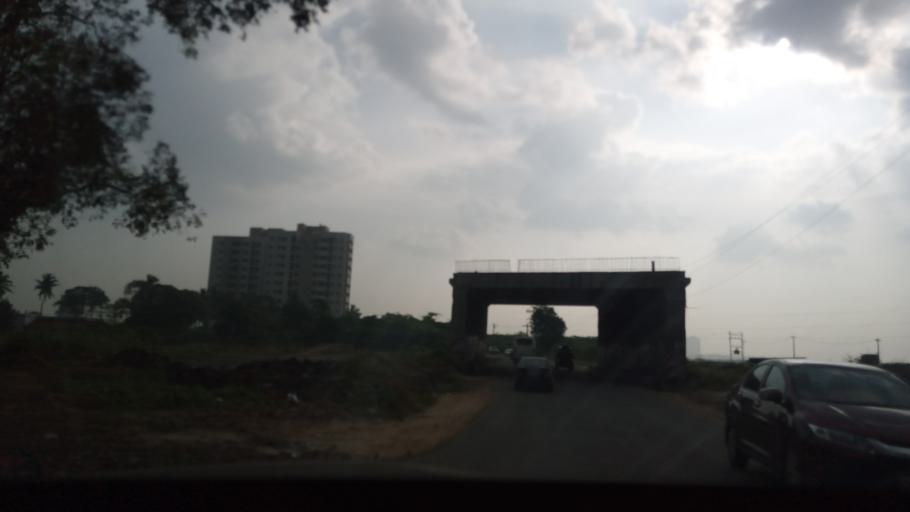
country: IN
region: Tamil Nadu
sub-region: Kancheepuram
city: Vengavasal
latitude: 12.7823
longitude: 80.2281
